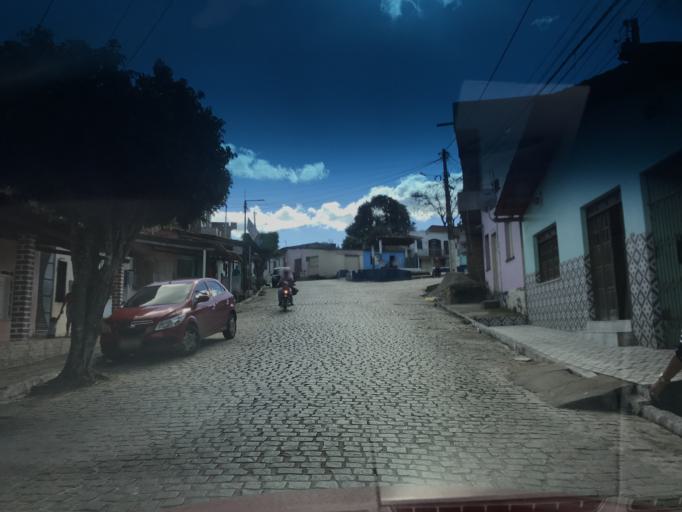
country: BR
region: Bahia
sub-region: Gandu
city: Gandu
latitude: -13.7458
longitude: -39.4920
